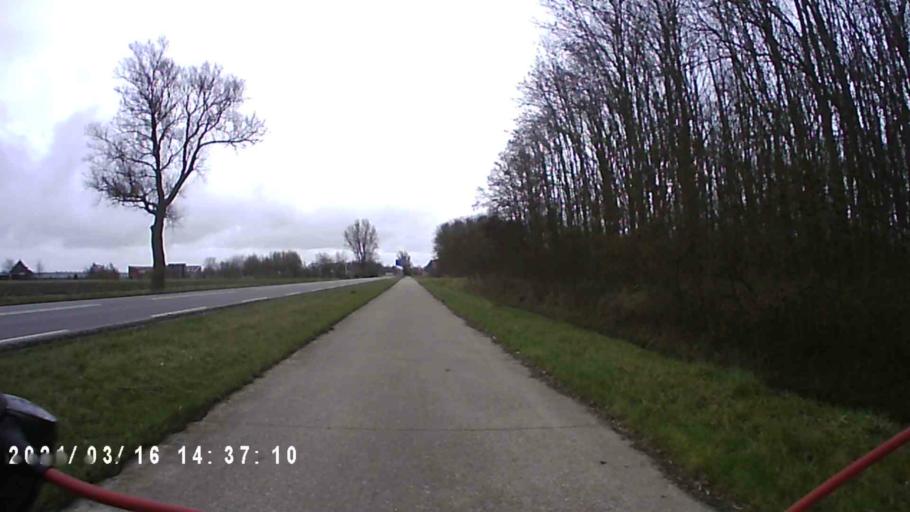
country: NL
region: Friesland
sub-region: Gemeente Harlingen
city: Harlingen
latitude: 53.1447
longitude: 5.4253
